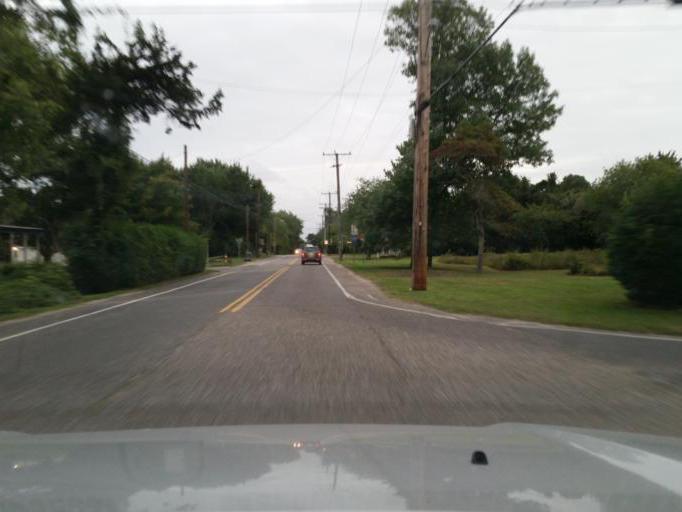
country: US
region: New Jersey
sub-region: Cape May County
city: West Cape May
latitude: 38.9428
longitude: -74.9629
